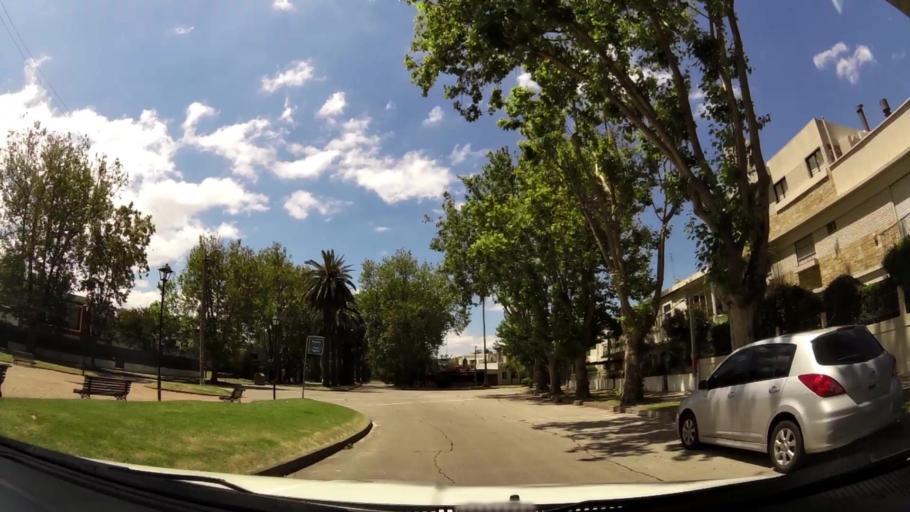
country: UY
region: Montevideo
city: Montevideo
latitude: -34.8681
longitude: -56.2005
